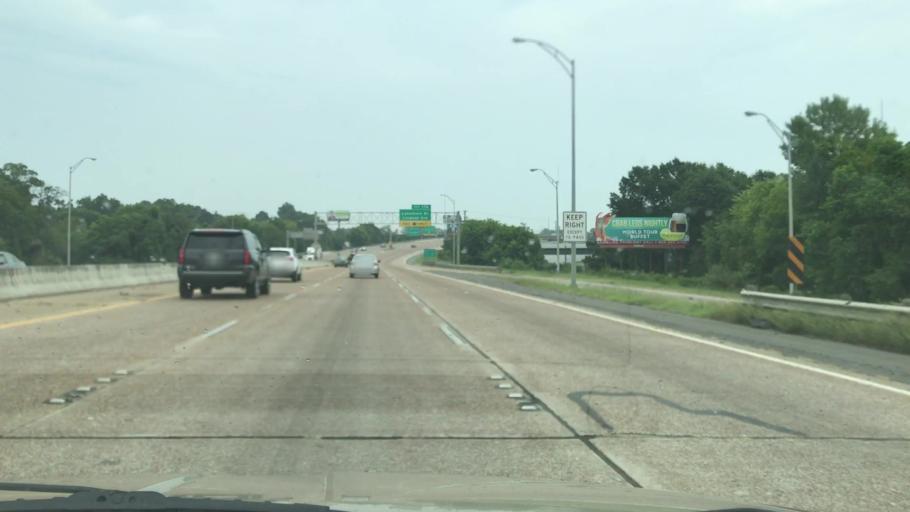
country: US
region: Louisiana
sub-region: Caddo Parish
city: Shreveport
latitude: 32.4868
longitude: -93.7734
